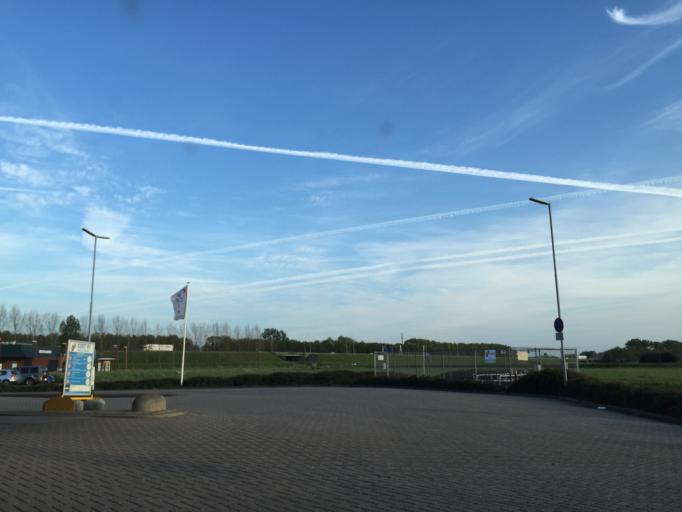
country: NL
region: North Holland
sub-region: Gemeente Hoorn
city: Hoorn
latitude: 52.6491
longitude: 5.0322
